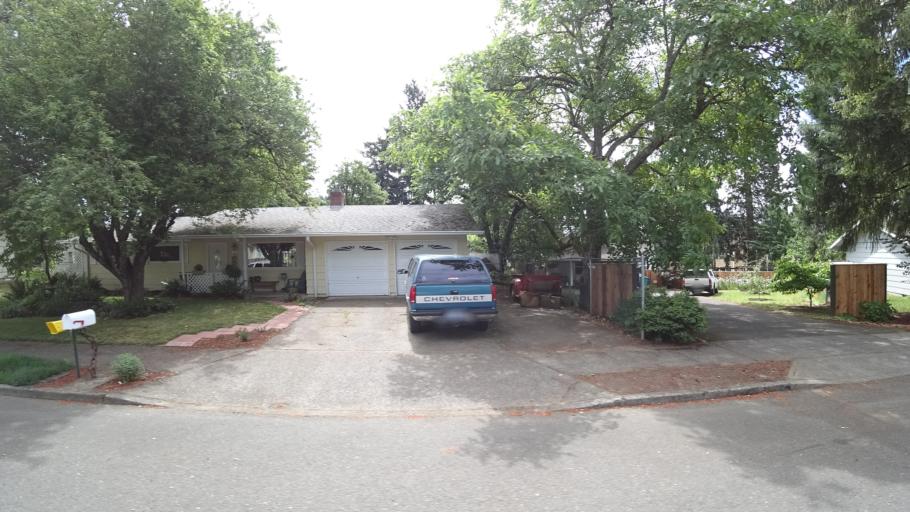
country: US
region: Oregon
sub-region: Multnomah County
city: Lents
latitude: 45.4916
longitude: -122.5257
